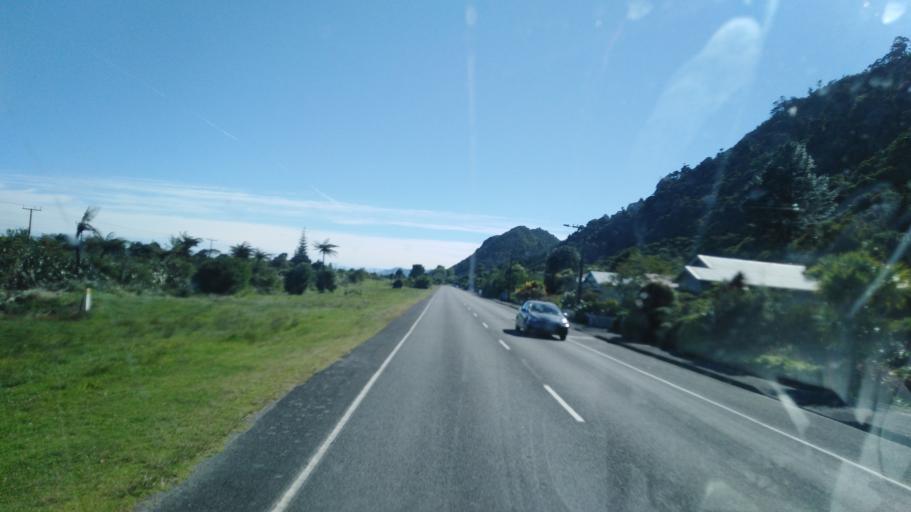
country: NZ
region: West Coast
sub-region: Buller District
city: Westport
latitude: -41.6363
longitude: 171.8485
